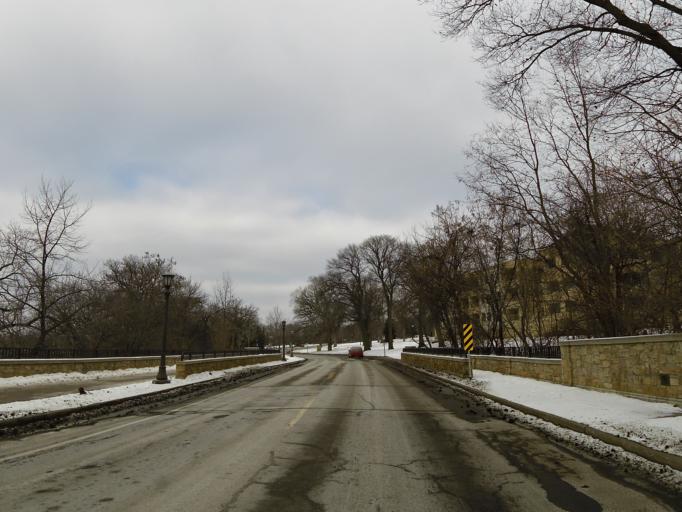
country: US
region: Minnesota
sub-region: Ramsey County
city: Lauderdale
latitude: 44.9388
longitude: -93.1975
